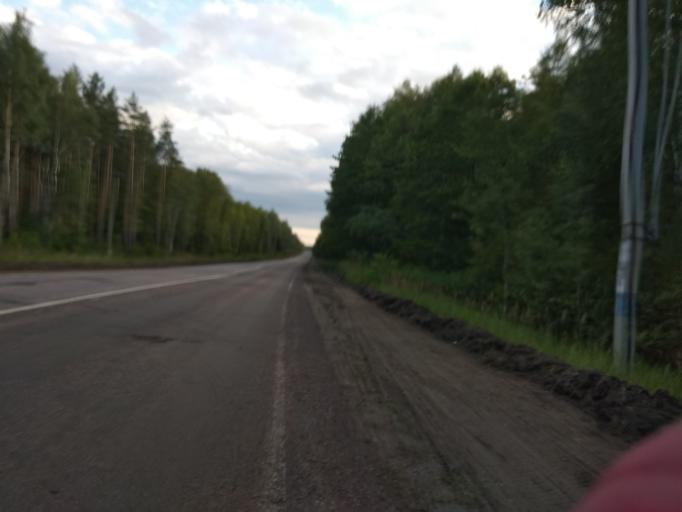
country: RU
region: Moskovskaya
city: Misheronskiy
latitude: 55.6434
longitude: 39.7562
